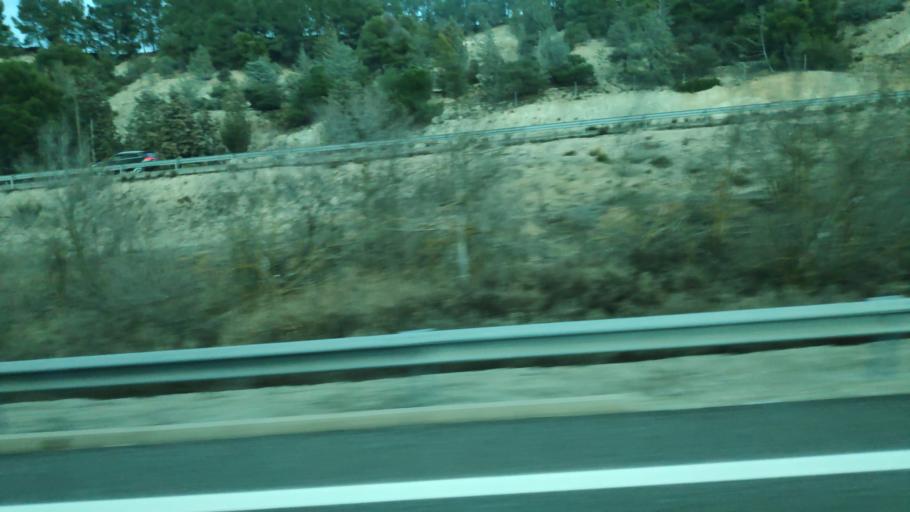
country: ES
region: Castille-La Mancha
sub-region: Provincia de Cuenca
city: Tarancon
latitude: 40.0204
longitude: -3.0342
